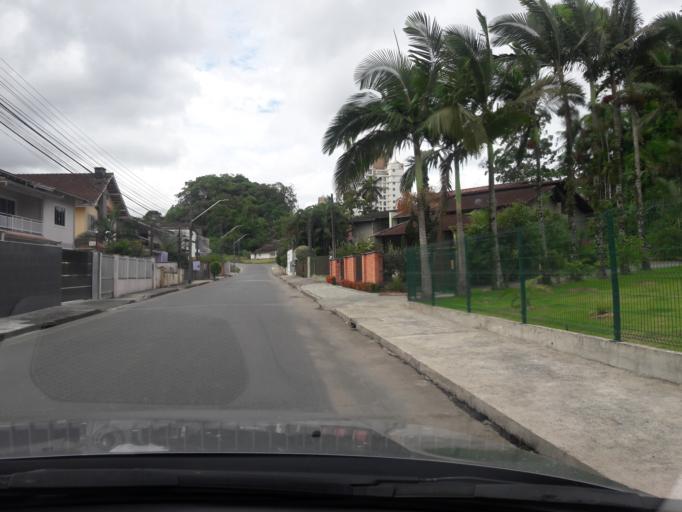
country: BR
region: Santa Catarina
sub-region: Joinville
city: Joinville
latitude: -26.3229
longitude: -48.8652
